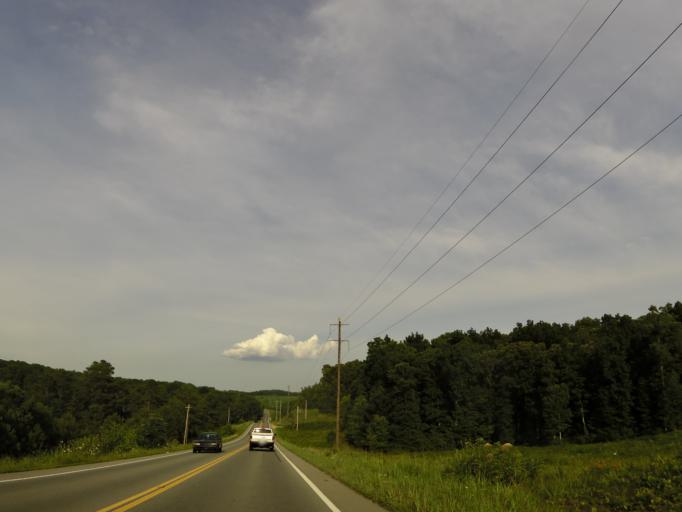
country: US
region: Tennessee
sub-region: Humphreys County
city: McEwen
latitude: 36.0936
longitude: -87.5612
